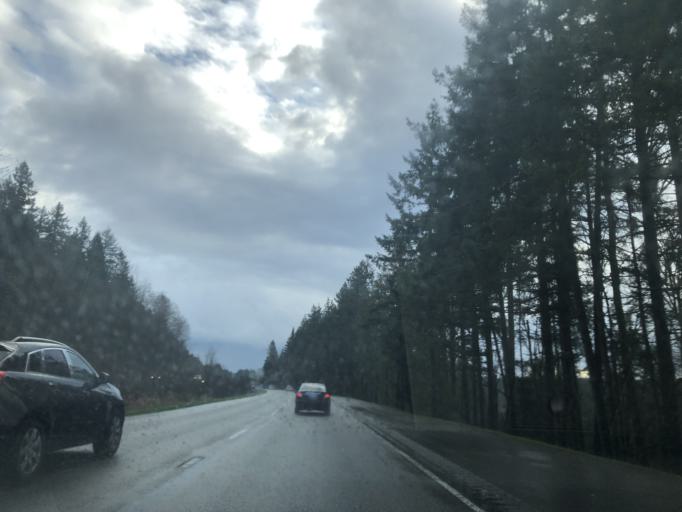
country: US
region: Washington
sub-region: Kitsap County
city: Burley
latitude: 47.4126
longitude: -122.6246
